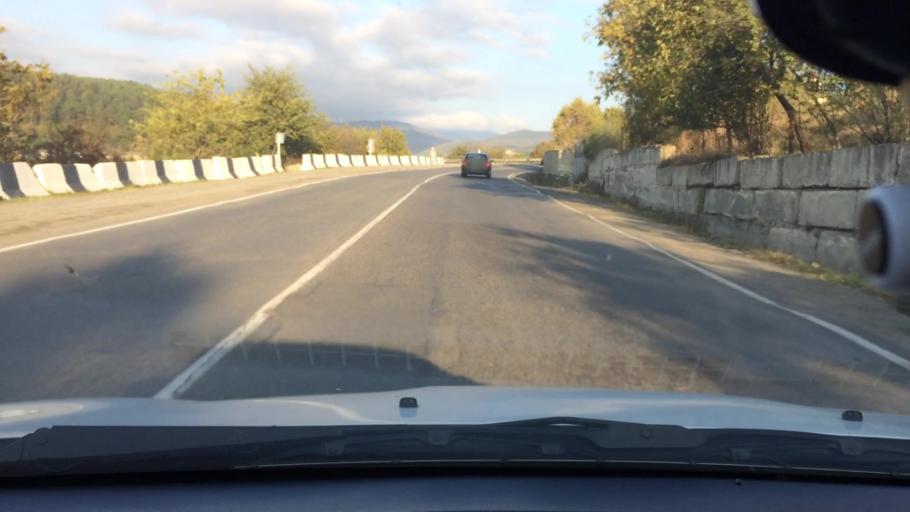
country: GE
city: Surami
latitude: 42.0175
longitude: 43.5682
